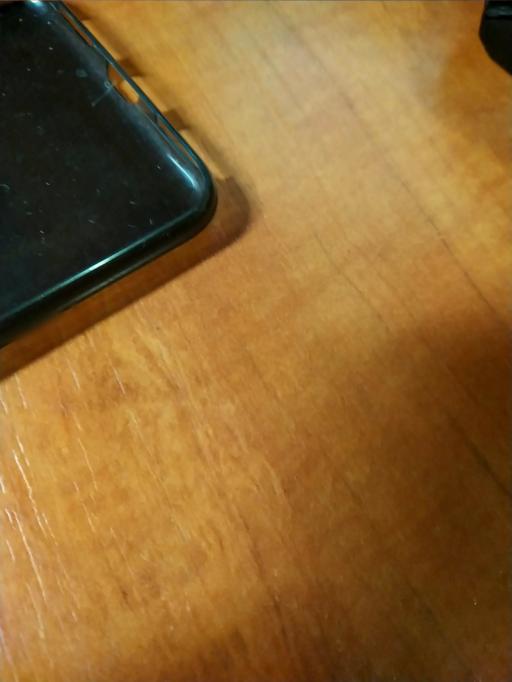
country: RU
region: Kaluga
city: Iznoski
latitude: 54.9236
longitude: 35.4007
